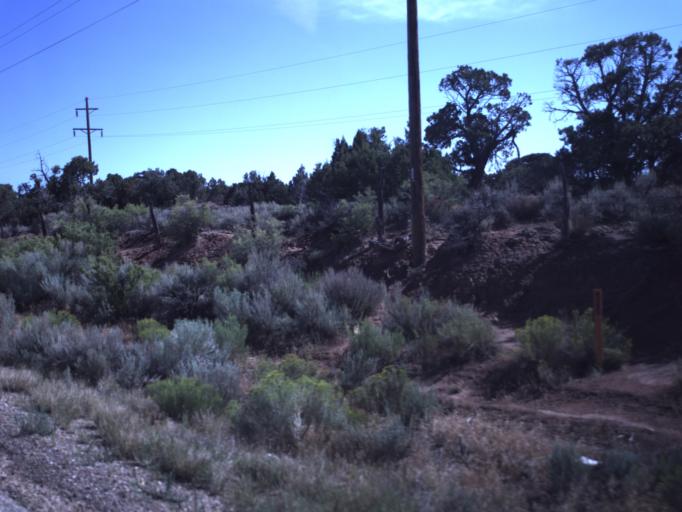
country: US
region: Utah
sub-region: Duchesne County
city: Duchesne
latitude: 40.2874
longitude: -110.3766
